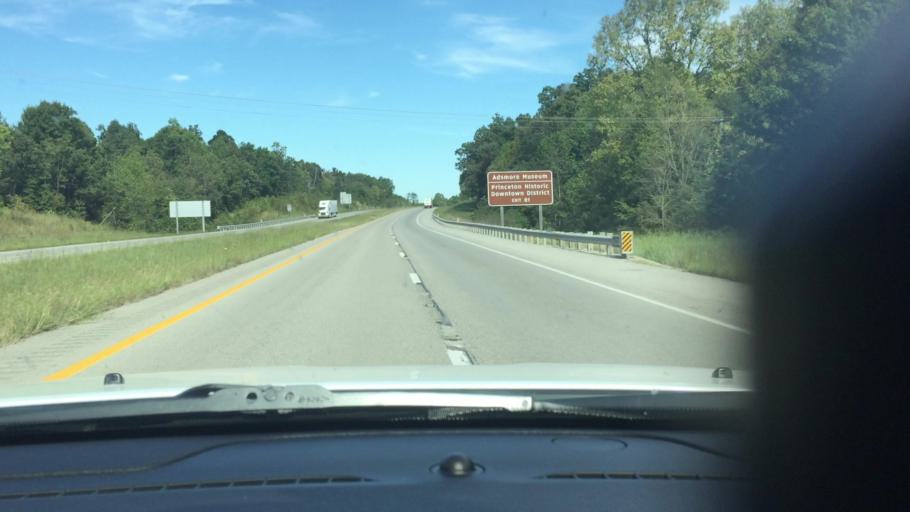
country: US
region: Kentucky
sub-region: Caldwell County
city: Princeton
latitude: 37.1280
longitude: -87.8815
